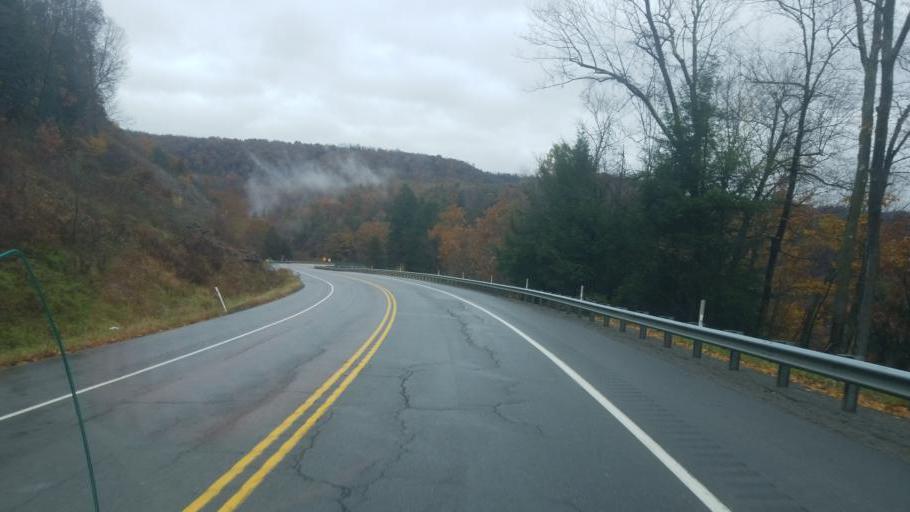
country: US
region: Pennsylvania
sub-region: Clearfield County
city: Clearfield
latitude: 41.0450
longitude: -78.3821
